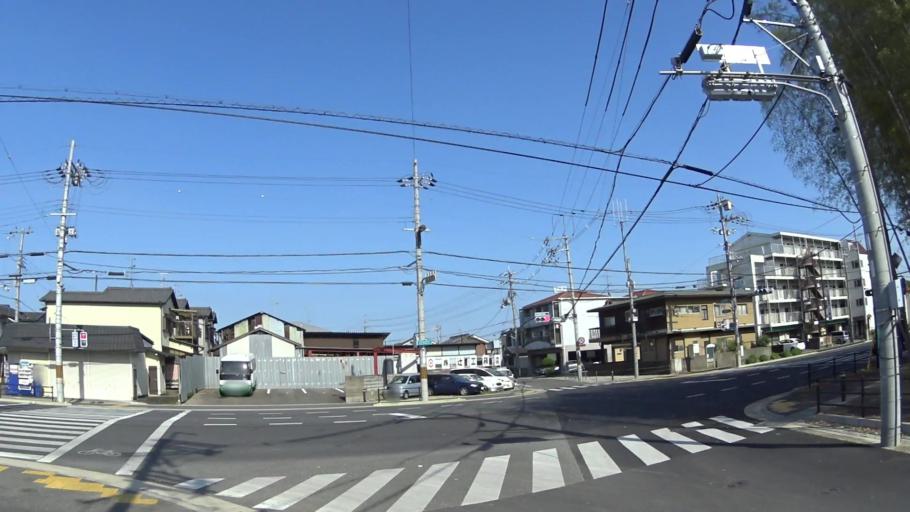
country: JP
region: Kyoto
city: Muko
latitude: 34.9429
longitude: 135.6855
